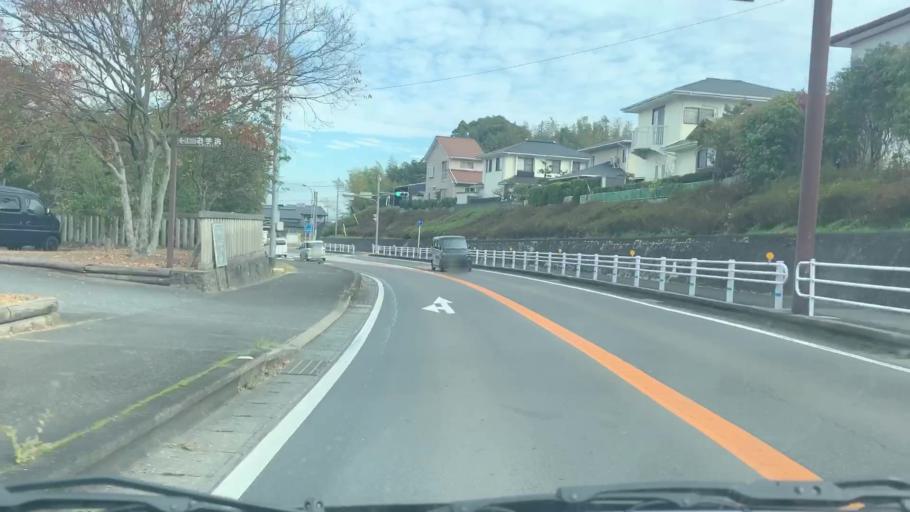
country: JP
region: Saga Prefecture
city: Karatsu
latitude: 33.3976
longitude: 129.9875
